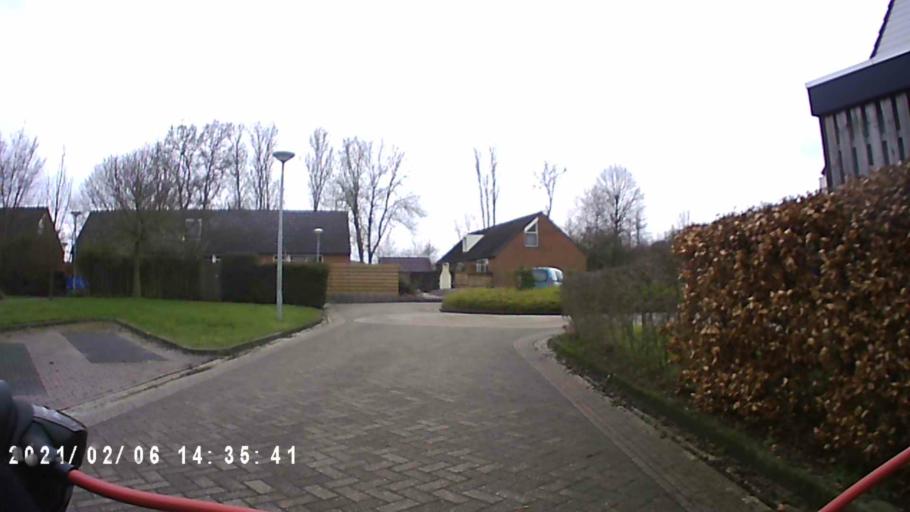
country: NL
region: Groningen
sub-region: Gemeente Winsum
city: Winsum
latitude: 53.3896
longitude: 6.5555
